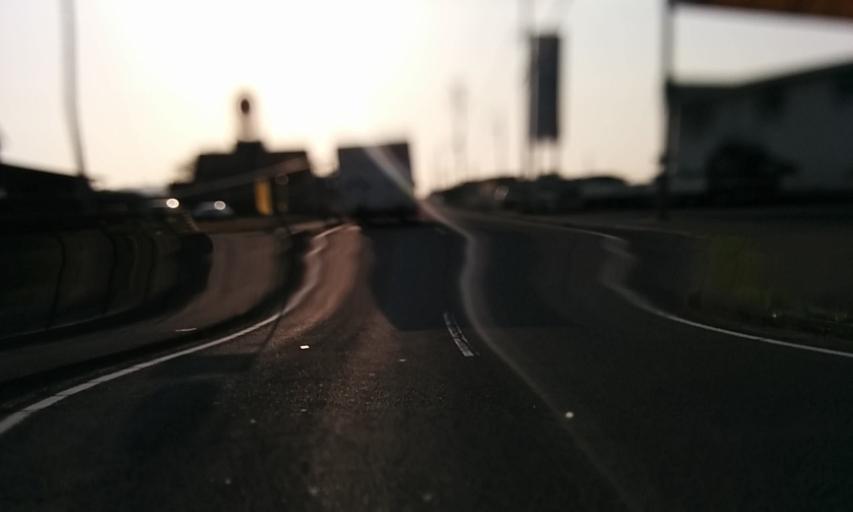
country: JP
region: Ehime
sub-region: Shikoku-chuo Shi
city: Matsuyama
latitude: 33.7777
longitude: 132.8354
